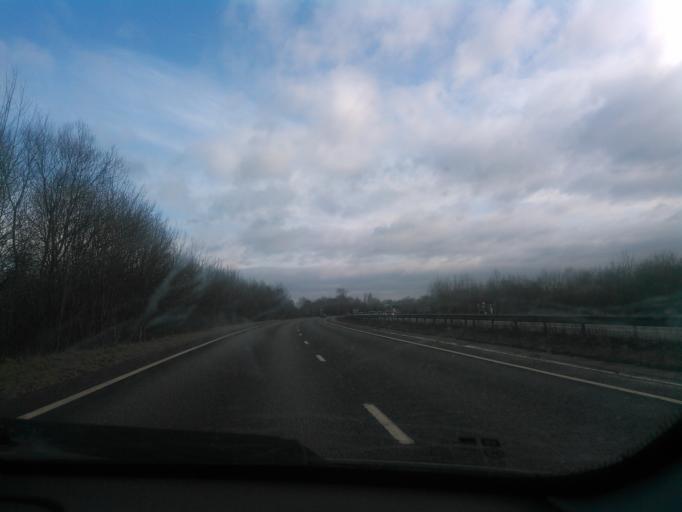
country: GB
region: England
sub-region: Derbyshire
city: Rodsley
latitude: 52.8851
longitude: -1.7335
